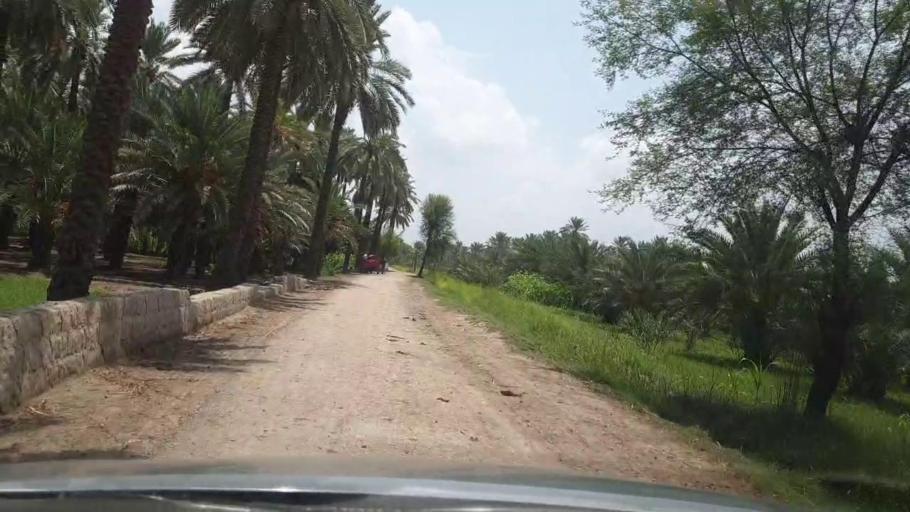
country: PK
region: Sindh
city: Khairpur
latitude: 27.6299
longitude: 68.7378
